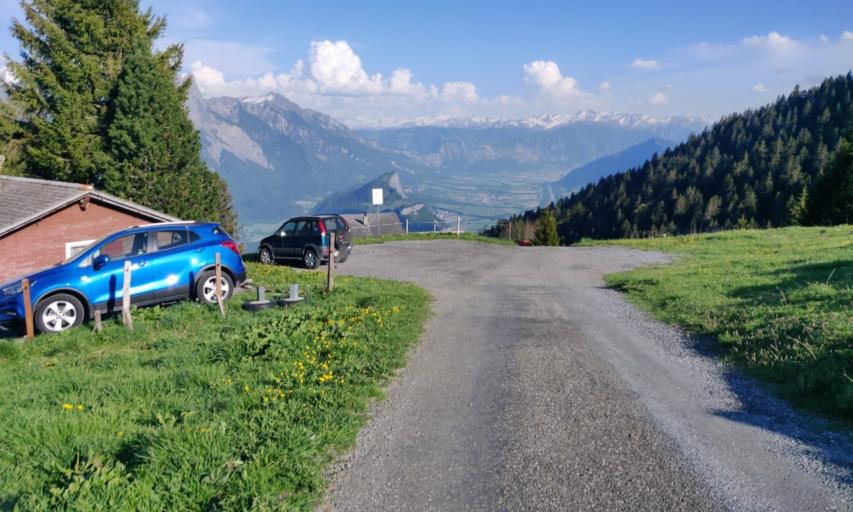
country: CH
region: Saint Gallen
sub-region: Wahlkreis Sarganserland
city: Sargans
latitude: 47.0772
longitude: 9.4374
